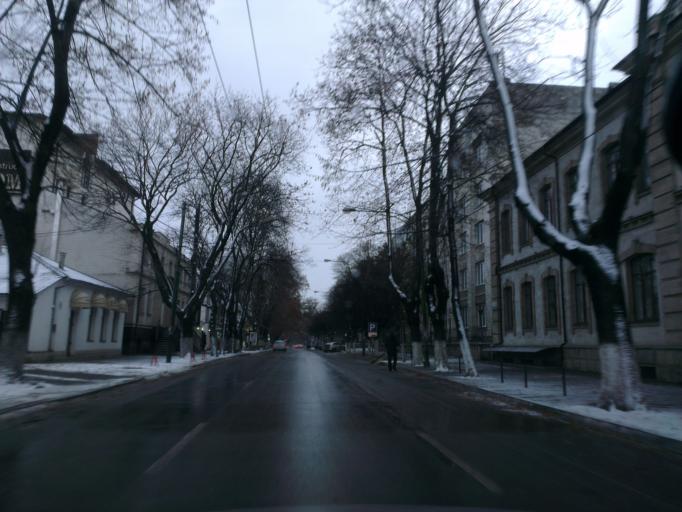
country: MD
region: Chisinau
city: Chisinau
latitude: 47.0202
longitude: 28.8243
